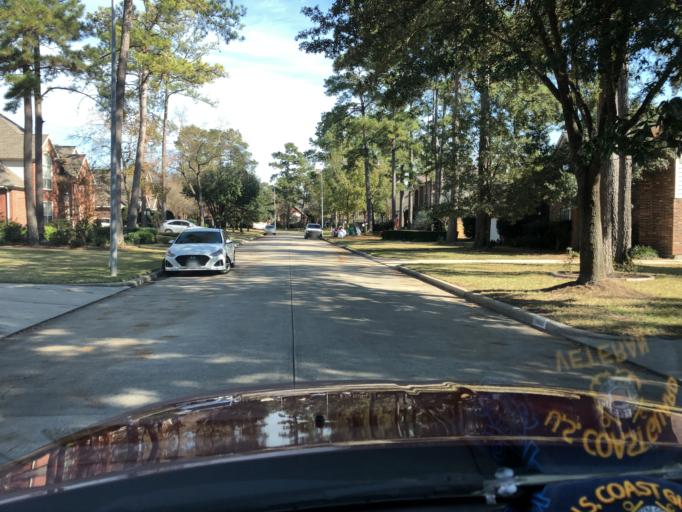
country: US
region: Texas
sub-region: Harris County
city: Tomball
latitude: 30.0192
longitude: -95.5520
